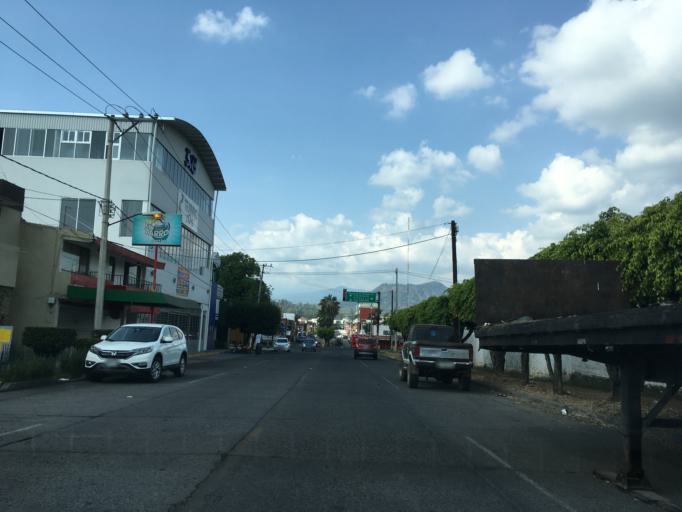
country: MX
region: Michoacan
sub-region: Uruapan
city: Uruapan
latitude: 19.3932
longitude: -102.0570
